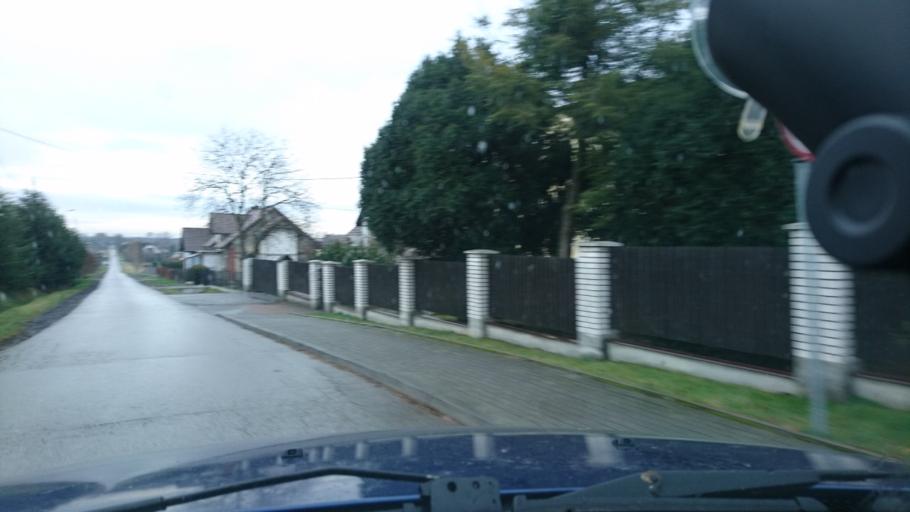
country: PL
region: Silesian Voivodeship
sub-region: Powiat bielski
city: Bestwinka
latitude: 49.9196
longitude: 19.0586
